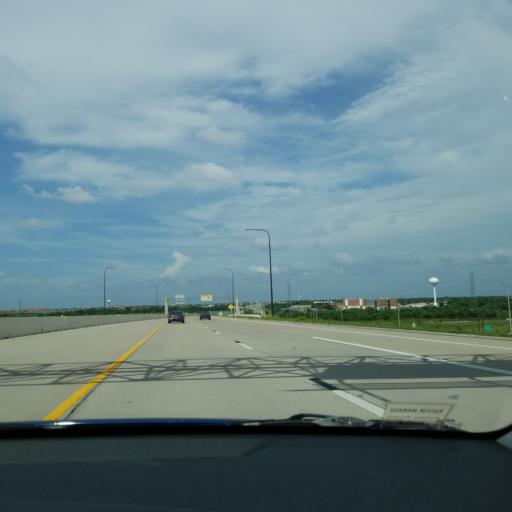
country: US
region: Texas
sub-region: Travis County
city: Manor
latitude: 30.3431
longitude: -97.5842
